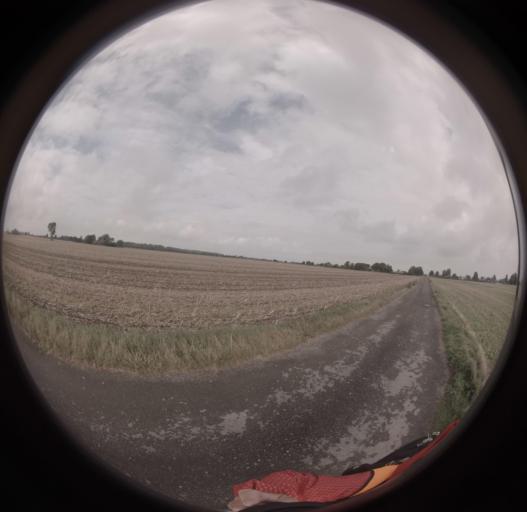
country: DK
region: South Denmark
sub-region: Nordfyns Kommune
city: Otterup
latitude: 55.5970
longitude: 10.3789
